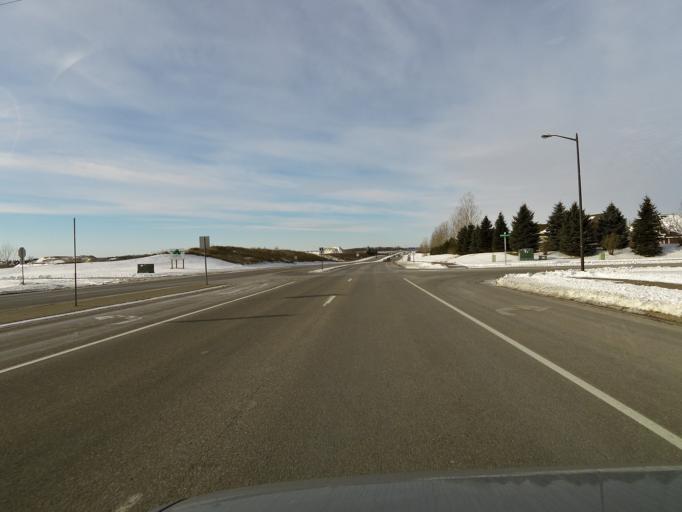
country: US
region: Minnesota
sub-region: Dakota County
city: Rosemount
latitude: 44.7173
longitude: -93.1561
